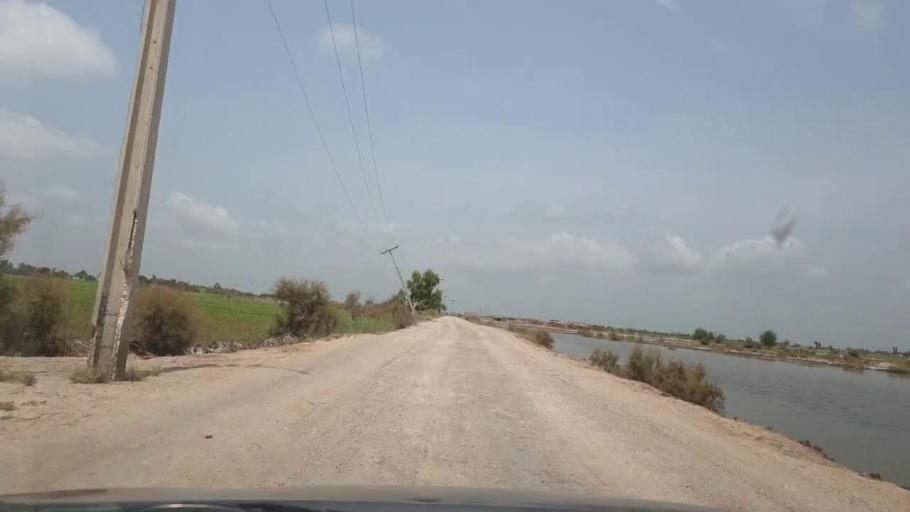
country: PK
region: Sindh
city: Ratodero
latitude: 27.9068
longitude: 68.3116
